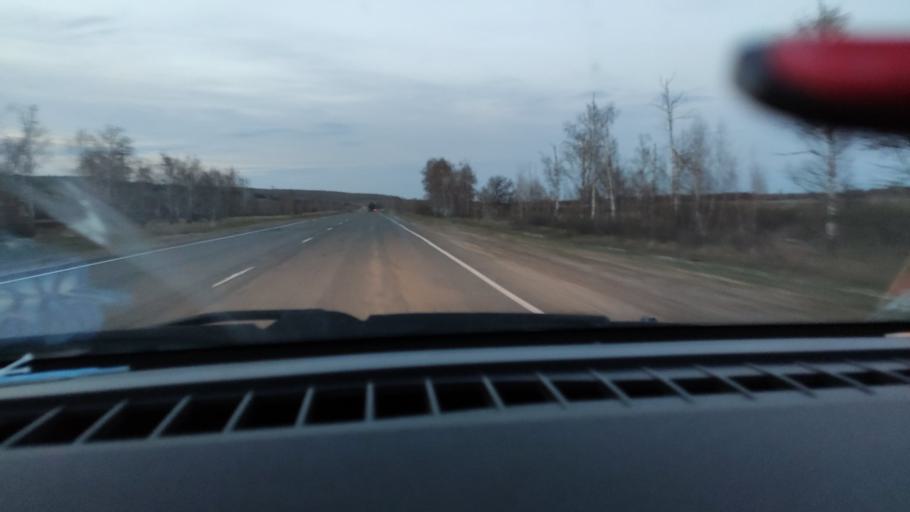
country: RU
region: Saratov
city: Sinodskoye
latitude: 52.0580
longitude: 46.7605
